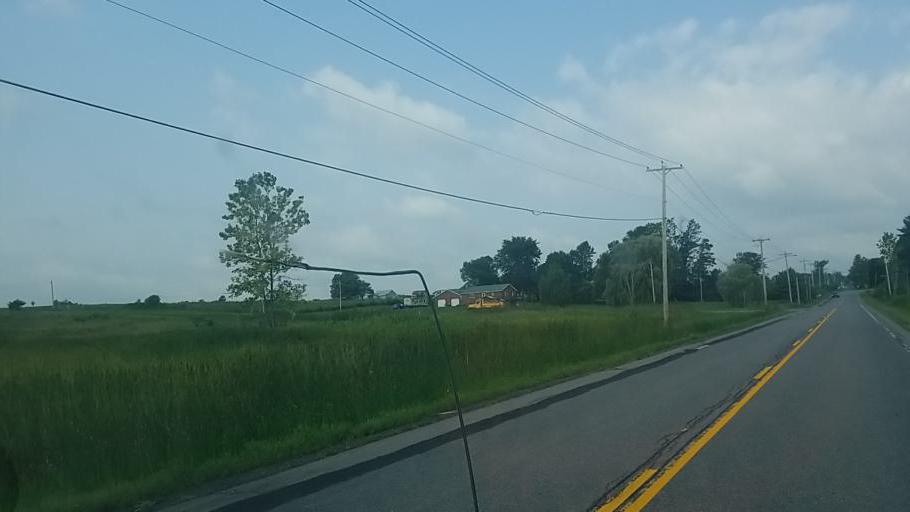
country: US
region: New York
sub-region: Fulton County
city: Johnstown
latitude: 43.0191
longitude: -74.4006
